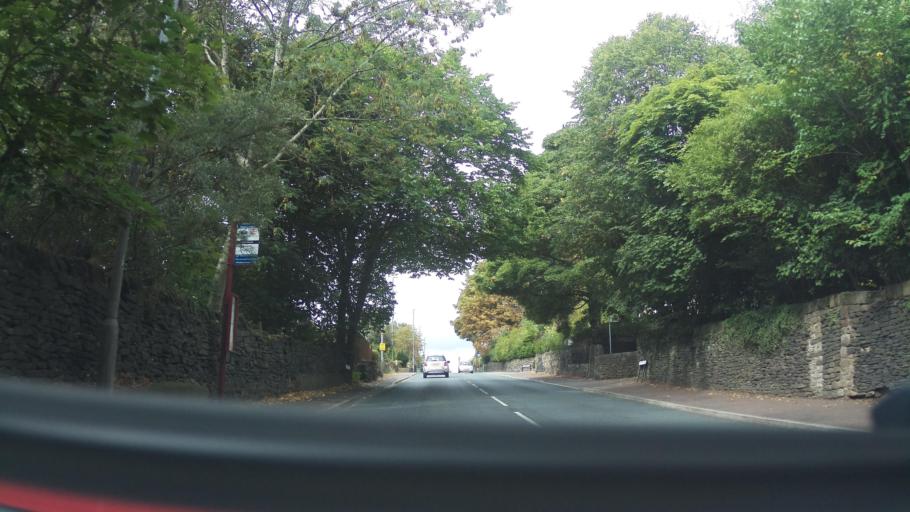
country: GB
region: England
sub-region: Kirklees
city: Holmfirth
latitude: 53.5790
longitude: -1.7650
